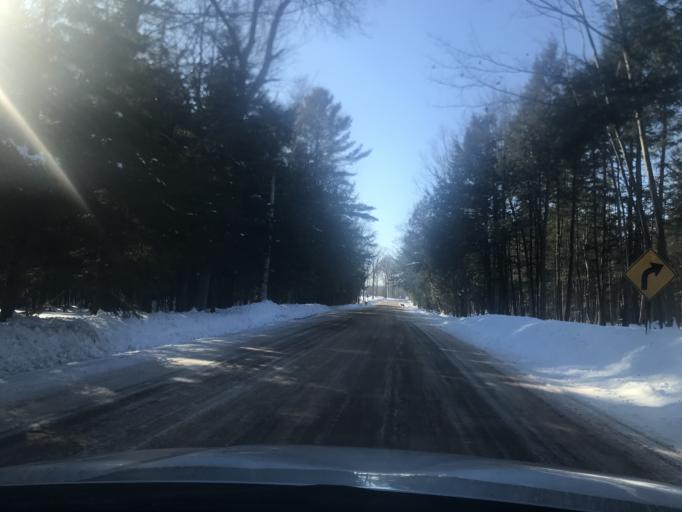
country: US
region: Wisconsin
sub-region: Marinette County
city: Marinette
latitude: 45.1378
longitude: -87.6709
